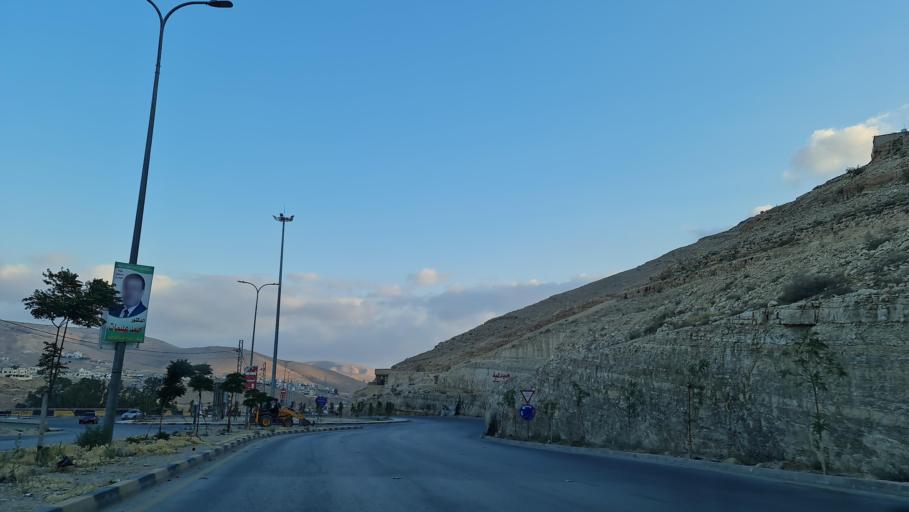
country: JO
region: Zarqa
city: Zarqa
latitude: 32.0810
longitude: 36.0695
